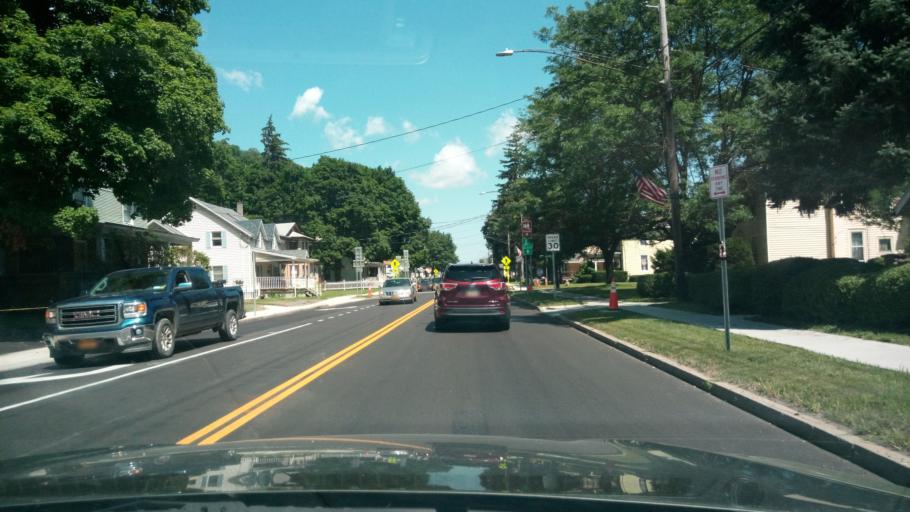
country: US
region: New York
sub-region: Schuyler County
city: Watkins Glen
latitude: 42.3722
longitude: -76.8690
